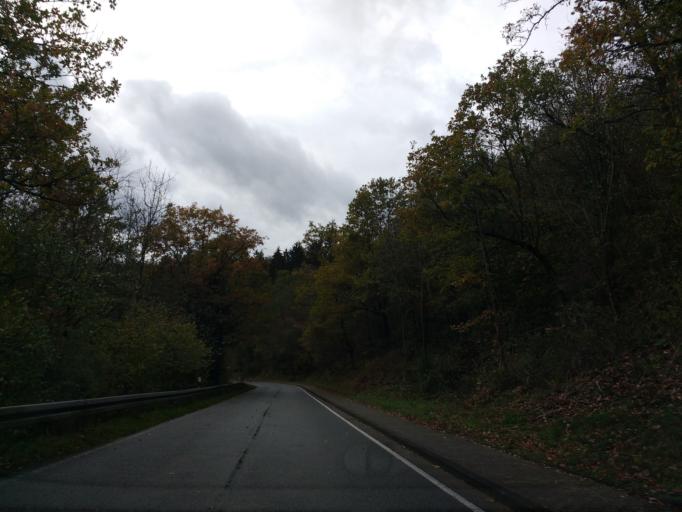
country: DE
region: Hesse
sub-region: Regierungsbezirk Kassel
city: Vohl
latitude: 51.2003
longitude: 8.9401
